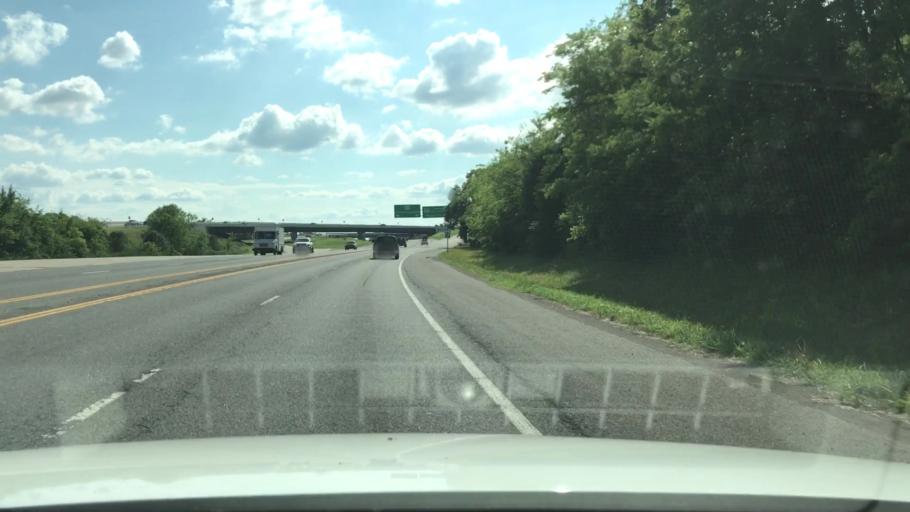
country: US
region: Tennessee
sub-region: Sumner County
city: Hendersonville
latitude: 36.3307
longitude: -86.5530
